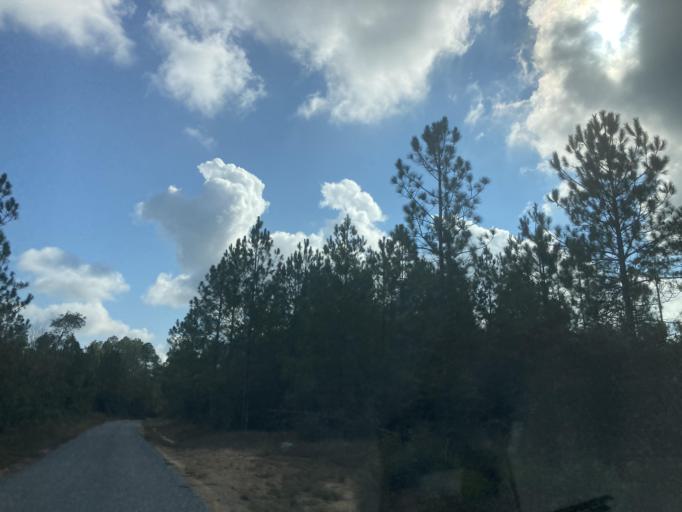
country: US
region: Mississippi
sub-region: Harrison County
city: Saucier
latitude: 30.7077
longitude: -89.2093
